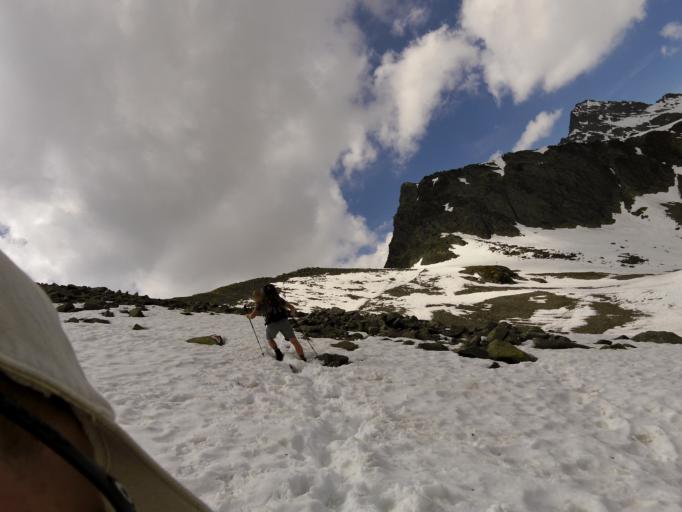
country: AT
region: Tyrol
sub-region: Politischer Bezirk Innsbruck Land
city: Neustift im Stubaital
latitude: 47.0742
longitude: 11.2084
